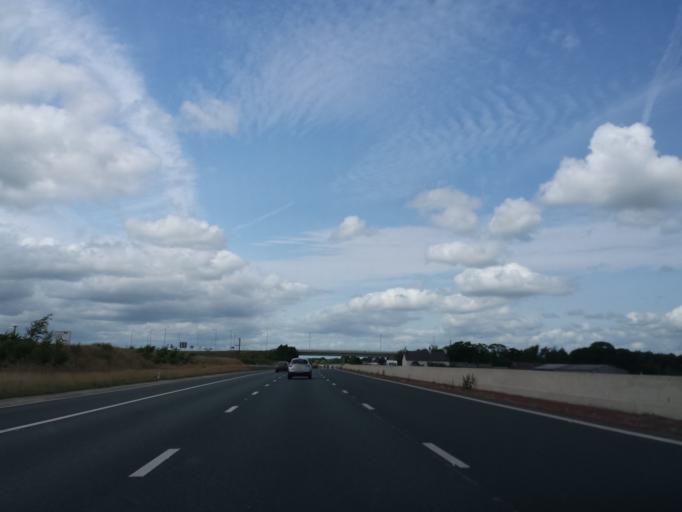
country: GB
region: England
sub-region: North Yorkshire
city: Bedale
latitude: 54.2699
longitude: -1.5243
